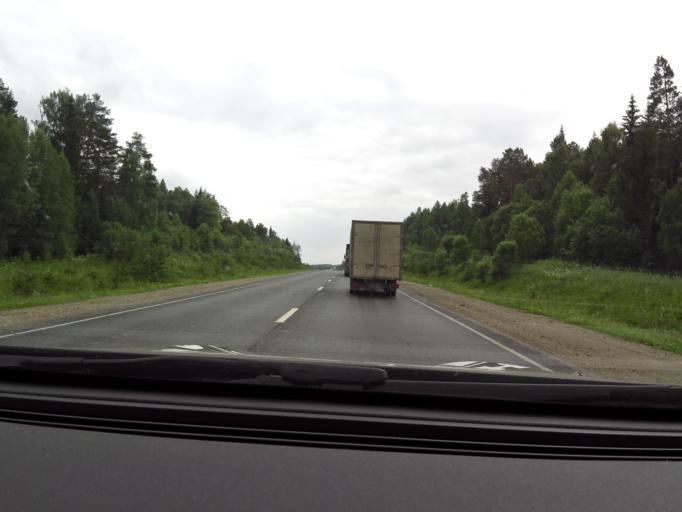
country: RU
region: Perm
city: Suksun
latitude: 57.1362
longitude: 57.2976
